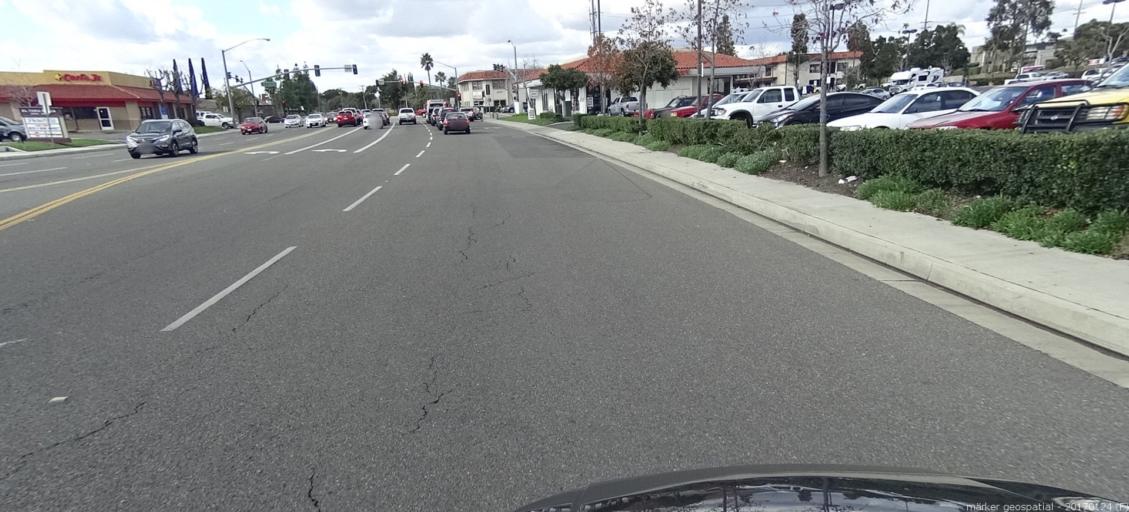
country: US
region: California
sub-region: Orange County
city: Laguna Hills
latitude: 33.6224
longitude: -117.6962
